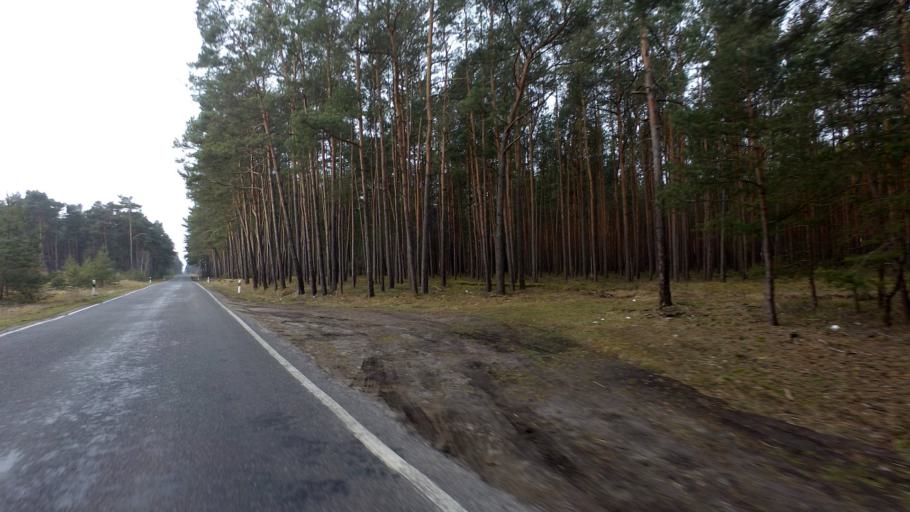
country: DE
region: Brandenburg
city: Borkheide
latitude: 52.1760
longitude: 12.8645
